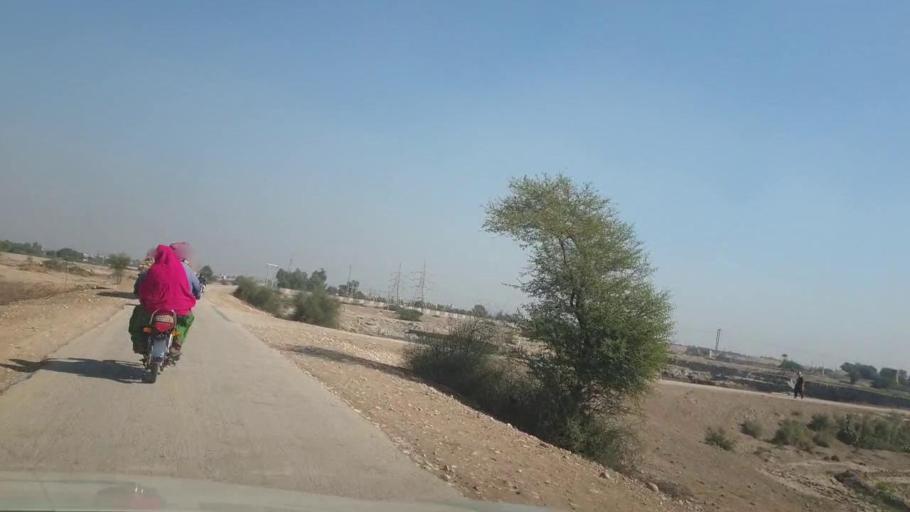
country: PK
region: Sindh
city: Bhan
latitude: 26.5460
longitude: 67.7087
